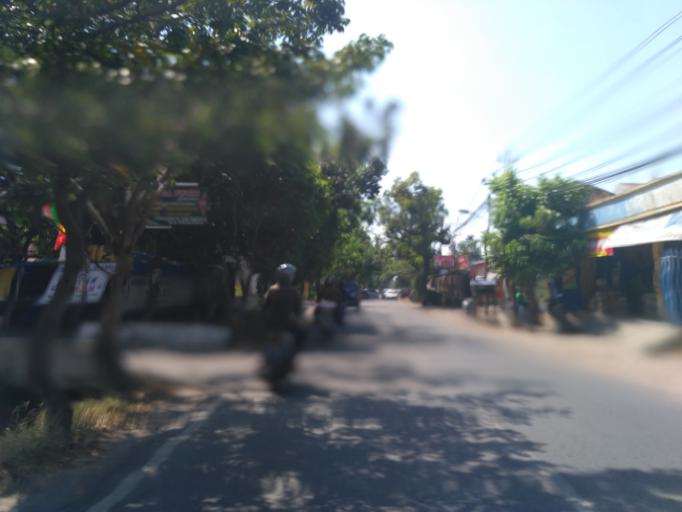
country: ID
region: Central Java
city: Semarang
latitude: -7.0068
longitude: 110.4428
